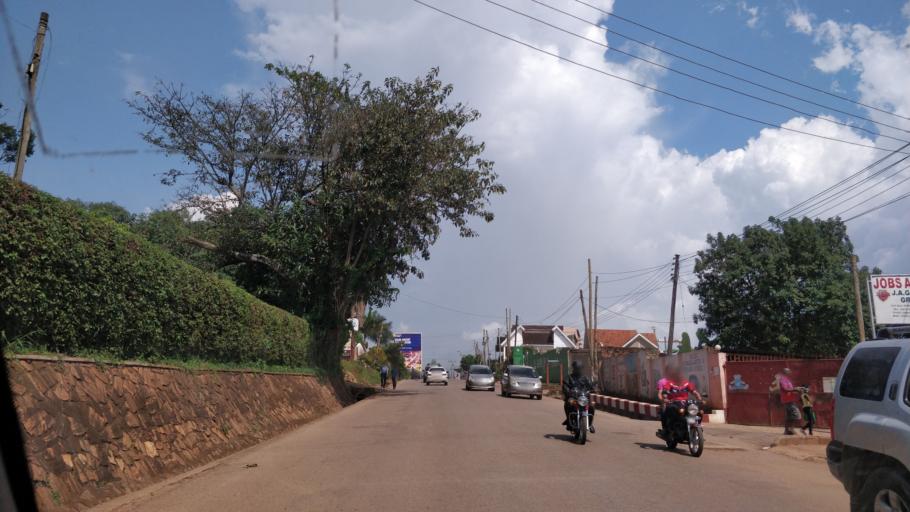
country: UG
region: Central Region
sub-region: Kampala District
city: Kampala
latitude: 0.2996
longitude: 32.6055
